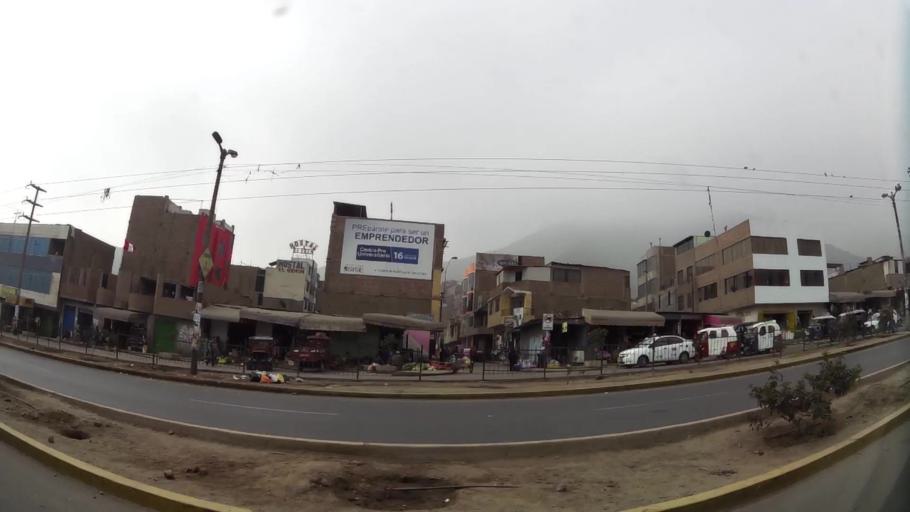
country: PE
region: Lima
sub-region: Lima
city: Chaclacayo
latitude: -12.0083
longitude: -76.8237
